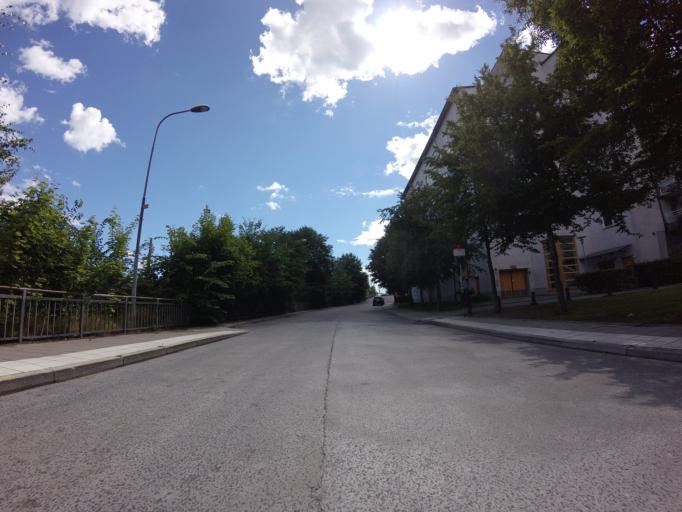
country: SE
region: Stockholm
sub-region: Stockholms Kommun
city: Stockholm
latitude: 59.3519
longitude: 18.0634
